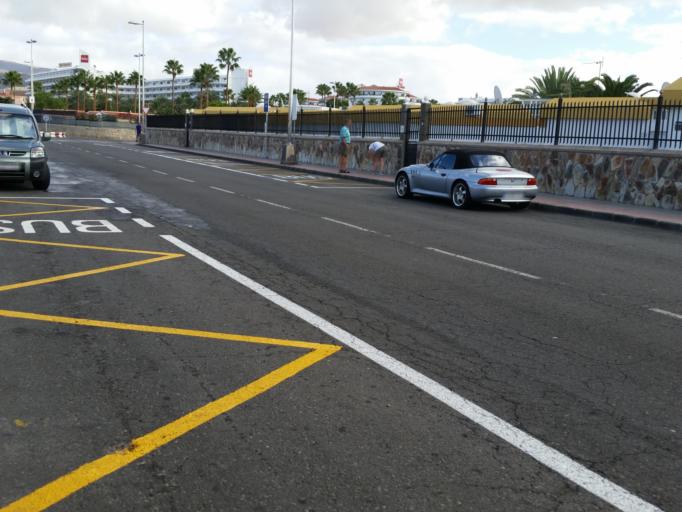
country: ES
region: Canary Islands
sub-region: Provincia de Las Palmas
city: Playa del Ingles
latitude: 27.7611
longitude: -15.5739
